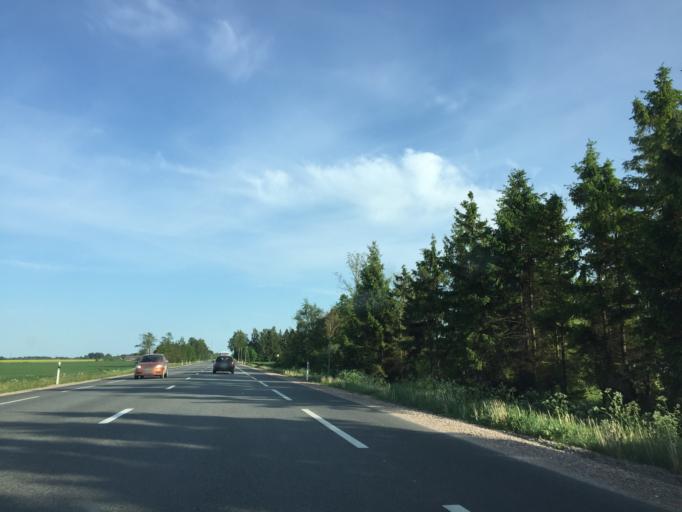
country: LV
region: Bauskas Rajons
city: Bauska
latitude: 56.4426
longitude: 24.1682
